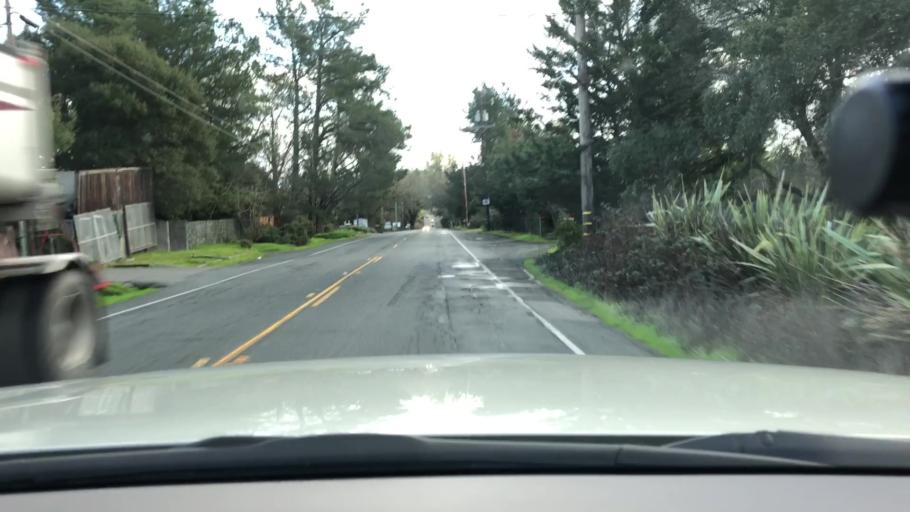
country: US
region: California
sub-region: Sonoma County
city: Forestville
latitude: 38.4587
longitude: -122.8744
